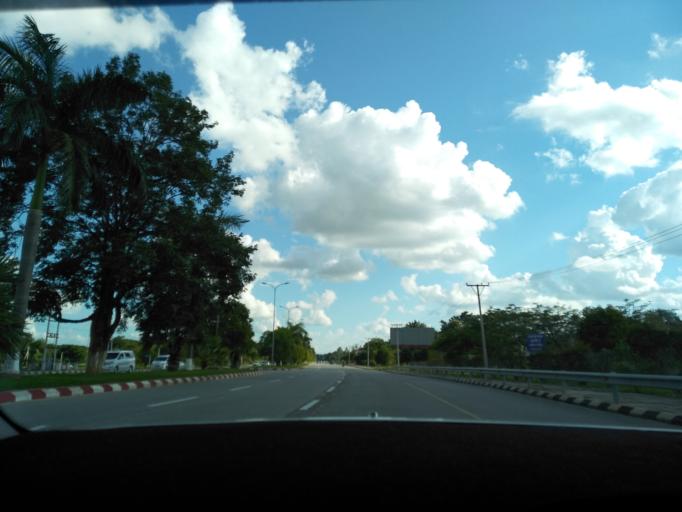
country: MM
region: Mandalay
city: Nay Pyi Taw
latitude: 19.7326
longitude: 96.1111
